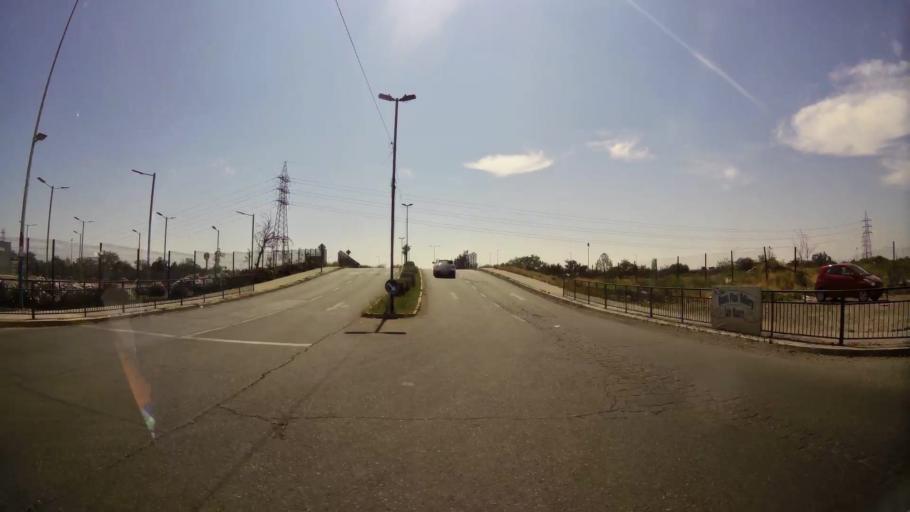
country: CL
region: Santiago Metropolitan
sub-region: Provincia de Santiago
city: Lo Prado
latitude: -33.4852
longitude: -70.7378
